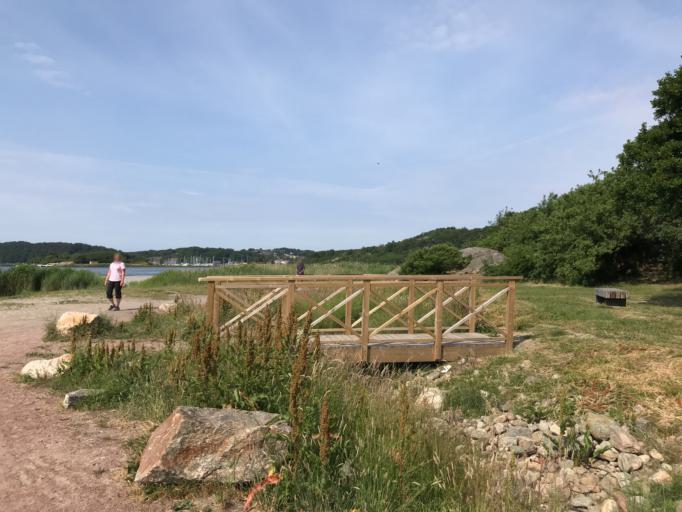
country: SE
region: Vaestra Goetaland
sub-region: Goteborg
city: Billdal
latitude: 57.6262
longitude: 11.9256
